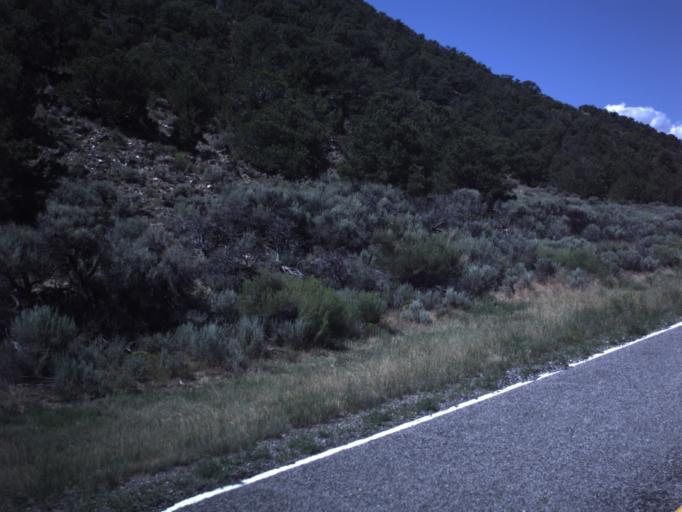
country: US
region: Utah
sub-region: Wayne County
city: Loa
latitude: 38.7576
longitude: -111.4087
